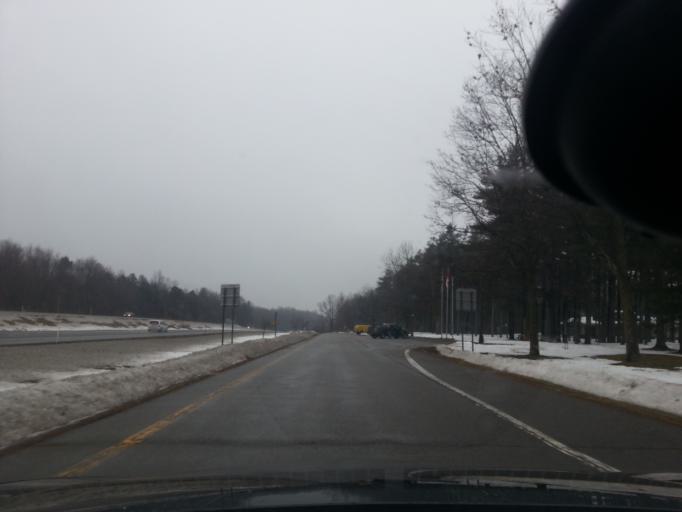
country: US
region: New York
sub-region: Jefferson County
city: Adams Center
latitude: 43.9027
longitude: -75.9829
